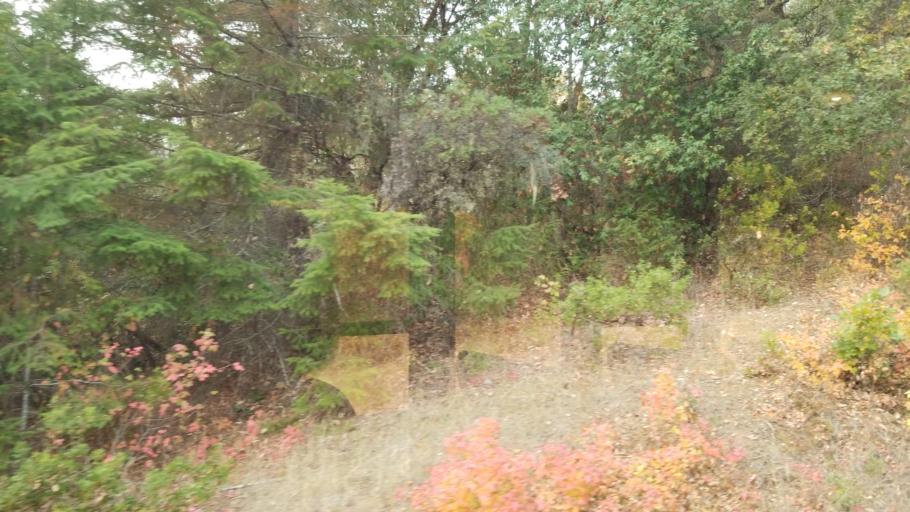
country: US
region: California
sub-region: Mendocino County
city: Willits
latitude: 39.4037
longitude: -123.3702
